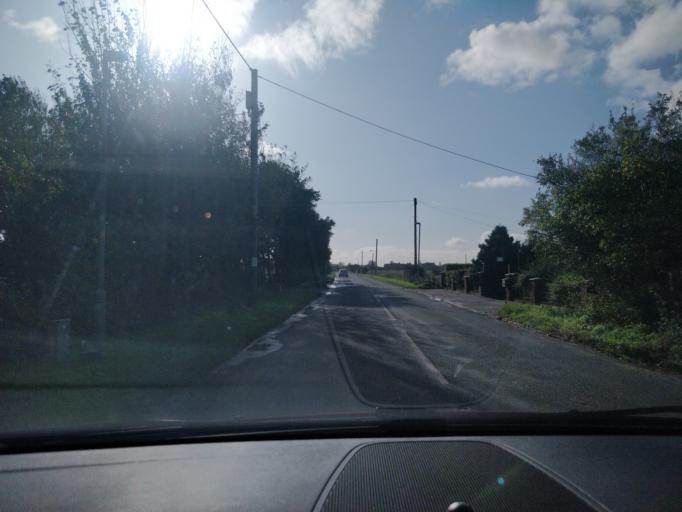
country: GB
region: England
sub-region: Lancashire
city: Banks
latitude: 53.6972
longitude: -2.8873
